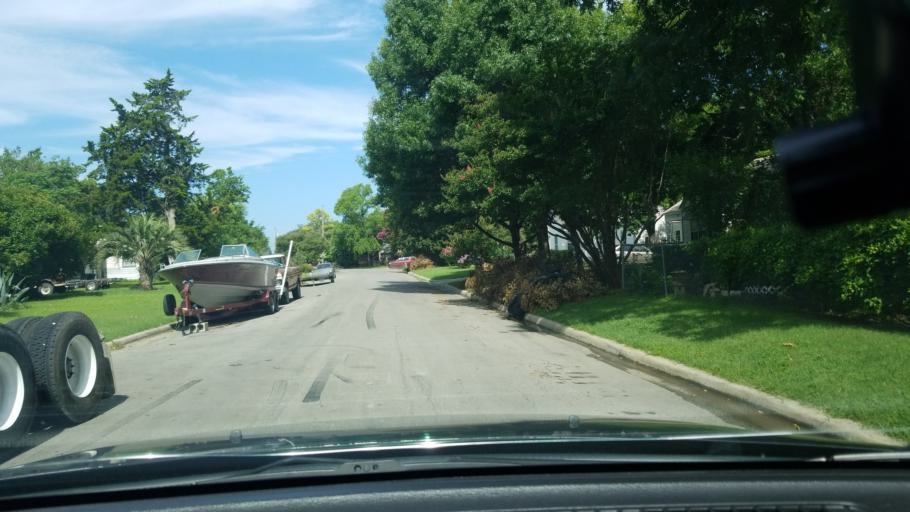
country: US
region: Texas
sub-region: Dallas County
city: Balch Springs
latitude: 32.7720
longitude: -96.6802
